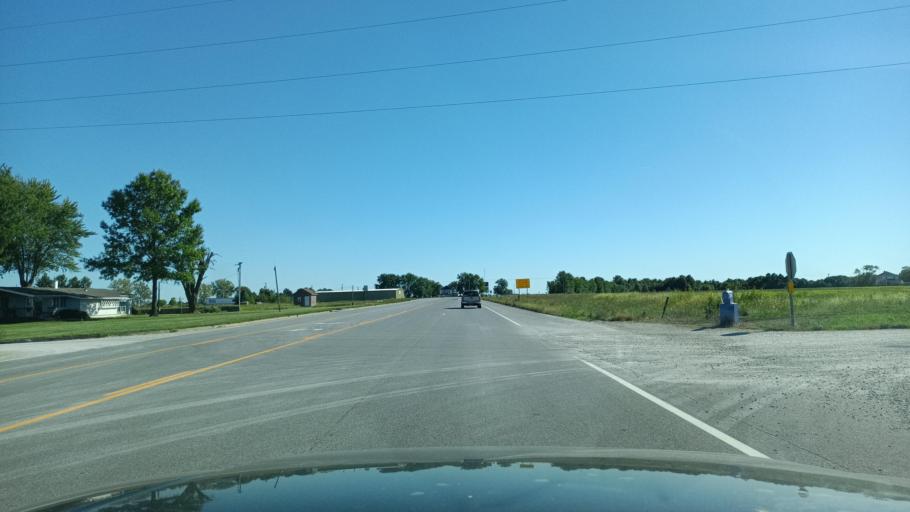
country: US
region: Missouri
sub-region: Macon County
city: Macon
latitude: 39.7163
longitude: -92.4647
